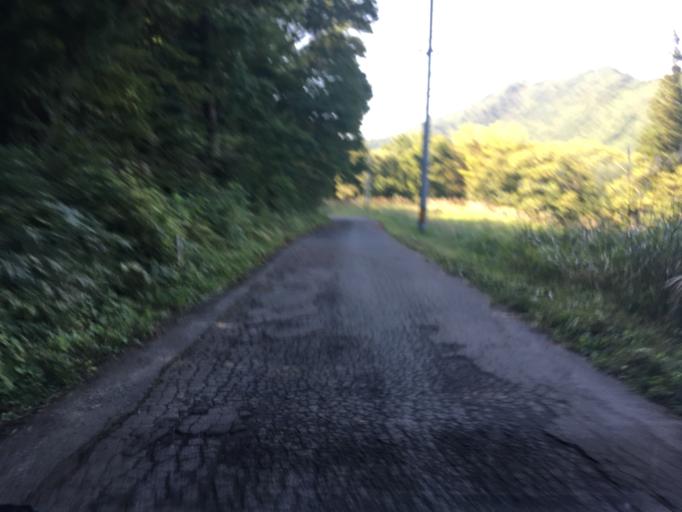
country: JP
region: Yamagata
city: Yonezawa
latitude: 37.8432
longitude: 140.1936
